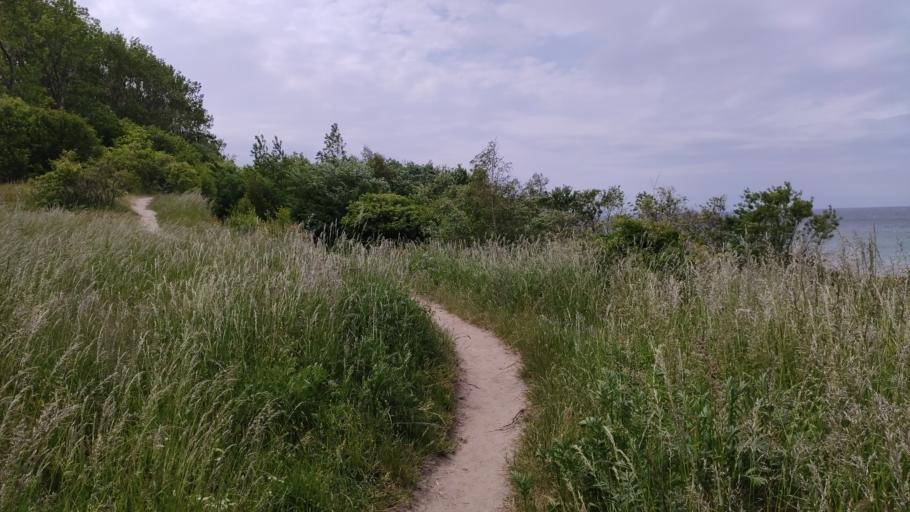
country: DE
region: Mecklenburg-Vorpommern
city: Bastorf
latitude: 54.1331
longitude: 11.6511
